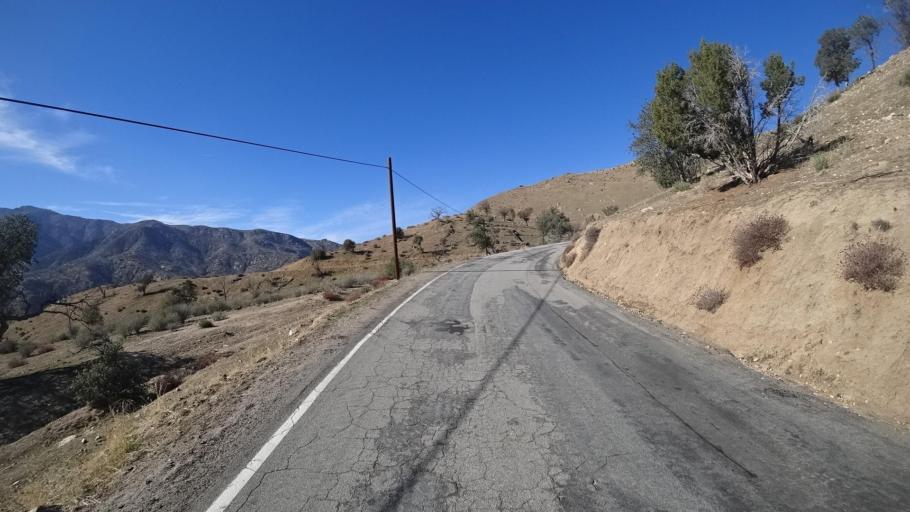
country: US
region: California
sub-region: Kern County
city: Bodfish
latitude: 35.5579
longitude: -118.5102
